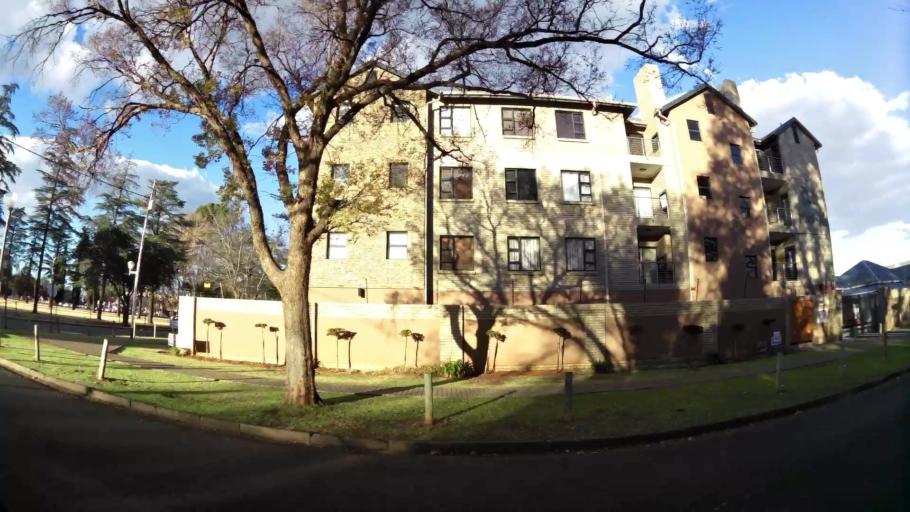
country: ZA
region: North-West
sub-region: Dr Kenneth Kaunda District Municipality
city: Potchefstroom
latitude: -26.6958
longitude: 27.0927
